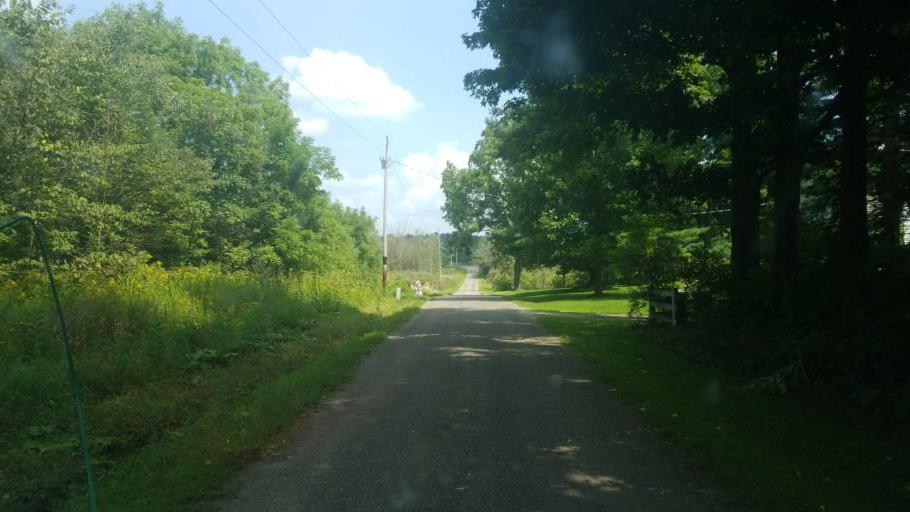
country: US
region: Ohio
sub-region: Huron County
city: New London
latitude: 41.0111
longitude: -82.4105
